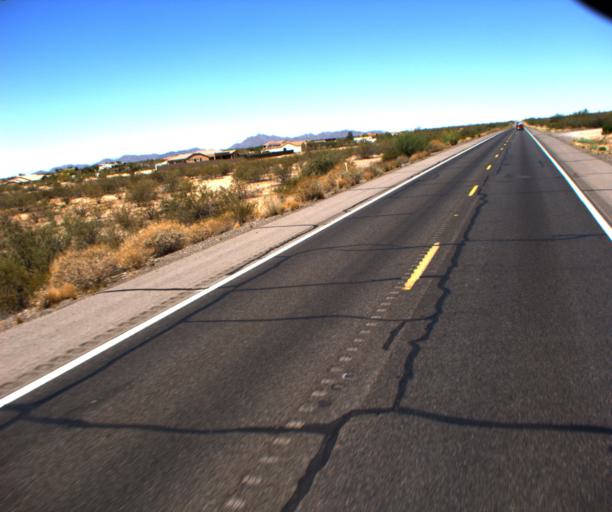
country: US
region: Arizona
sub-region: Yavapai County
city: Congress
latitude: 34.0404
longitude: -112.8313
